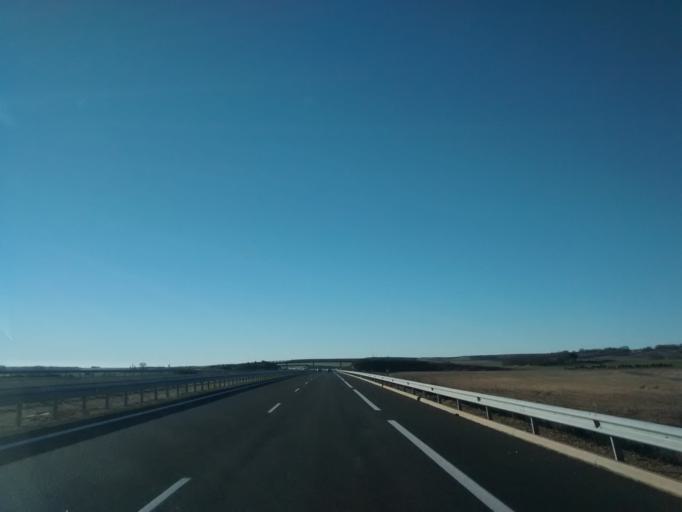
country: ES
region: Castille and Leon
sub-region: Provincia de Palencia
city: Espinosa de Villagonzalo
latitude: 42.4963
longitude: -4.3818
